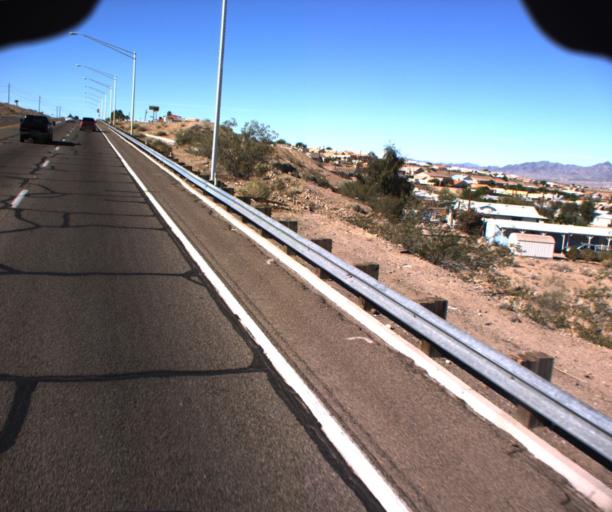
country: US
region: Arizona
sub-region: Mohave County
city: Bullhead City
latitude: 35.0460
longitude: -114.5897
